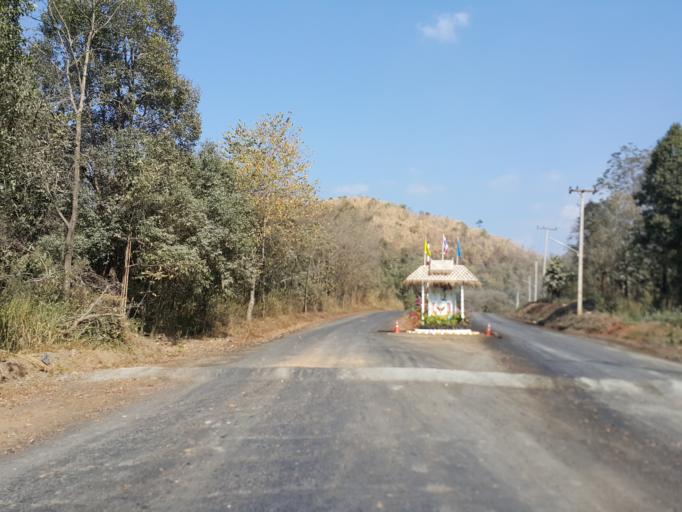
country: TH
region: Chiang Mai
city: Mae On
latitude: 18.8397
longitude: 99.2257
